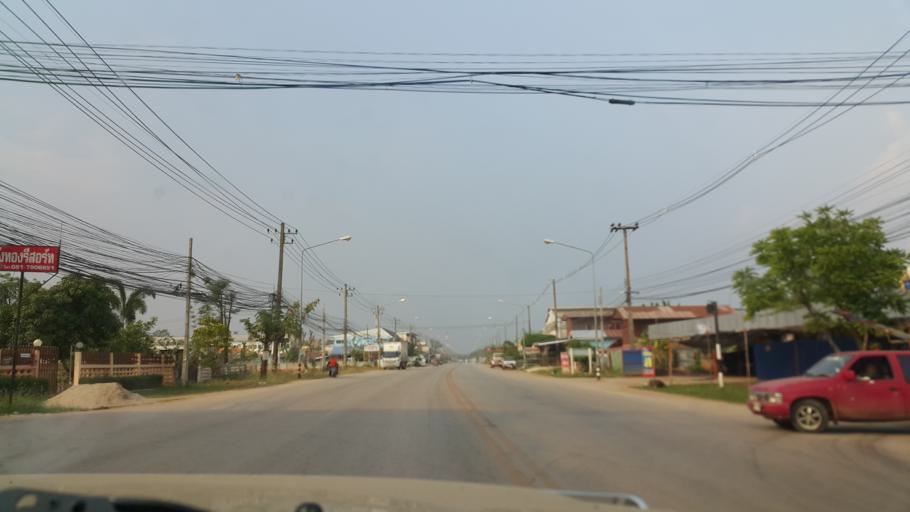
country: TH
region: Nakhon Phanom
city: That Phanom
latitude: 16.9447
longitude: 104.7210
